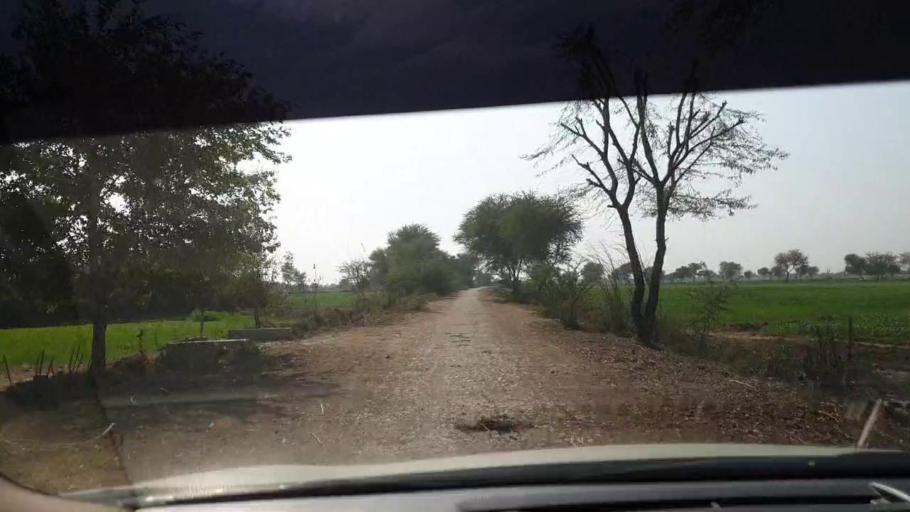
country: PK
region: Sindh
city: Berani
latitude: 25.8130
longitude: 68.7591
